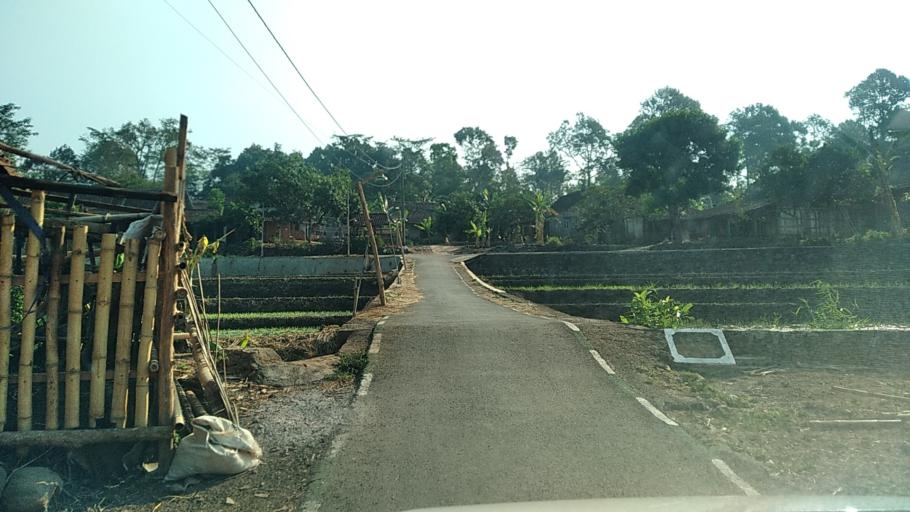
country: ID
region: Central Java
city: Semarang
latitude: -7.0233
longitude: 110.2900
